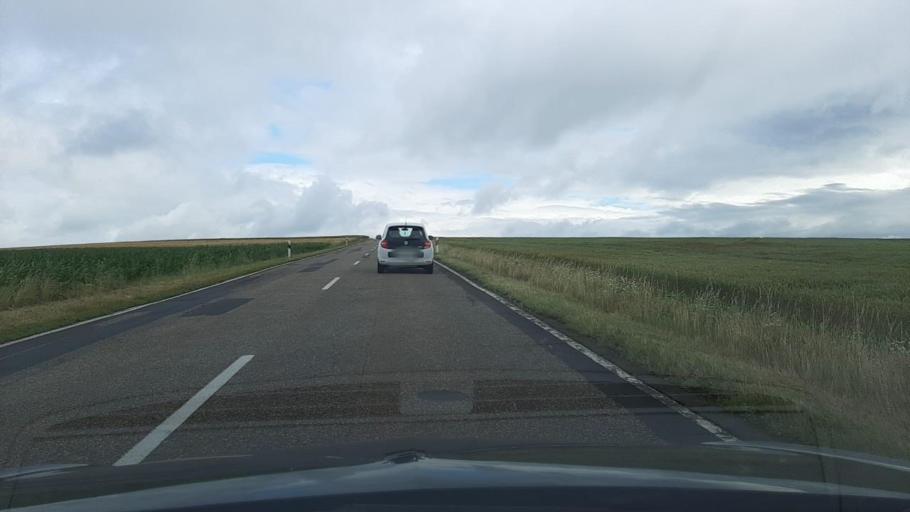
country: DE
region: Rheinland-Pfalz
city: Kerben
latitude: 50.3188
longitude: 7.3865
